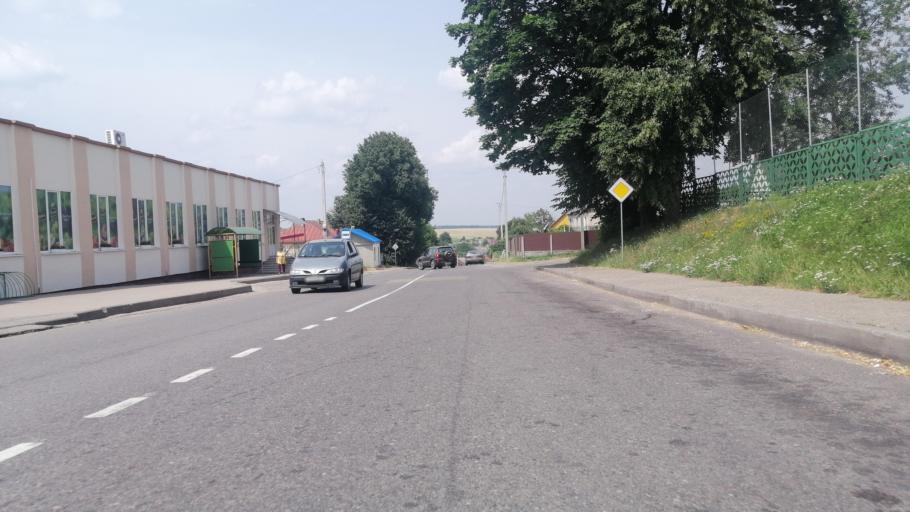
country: BY
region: Grodnenskaya
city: Navahrudak
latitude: 53.6036
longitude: 25.8239
